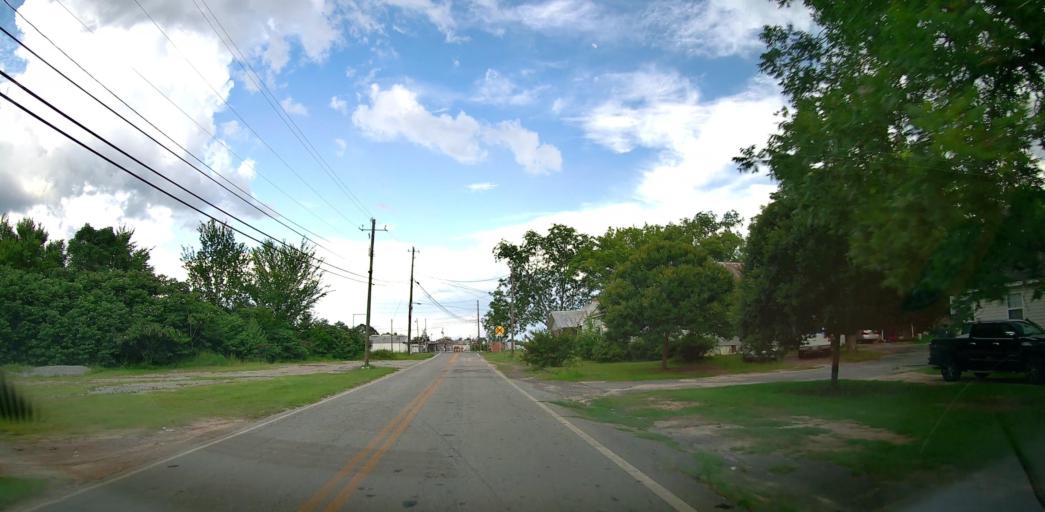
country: US
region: Georgia
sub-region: Bleckley County
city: Cochran
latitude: 32.3920
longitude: -83.3612
